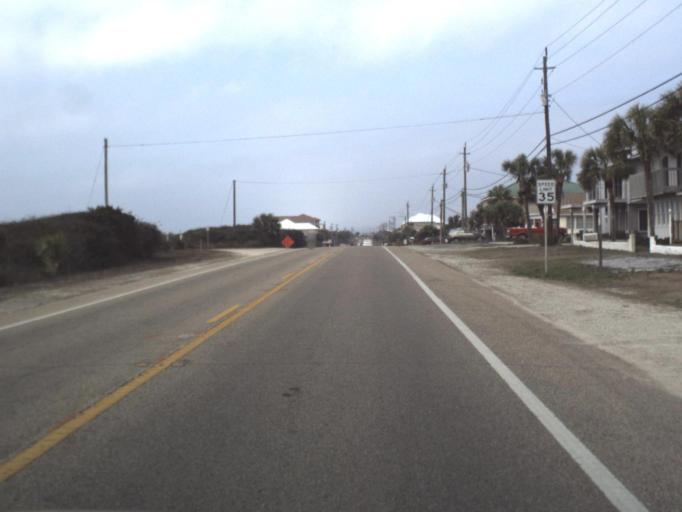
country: US
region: Florida
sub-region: Bay County
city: Laguna Beach
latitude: 30.2508
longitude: -85.9493
